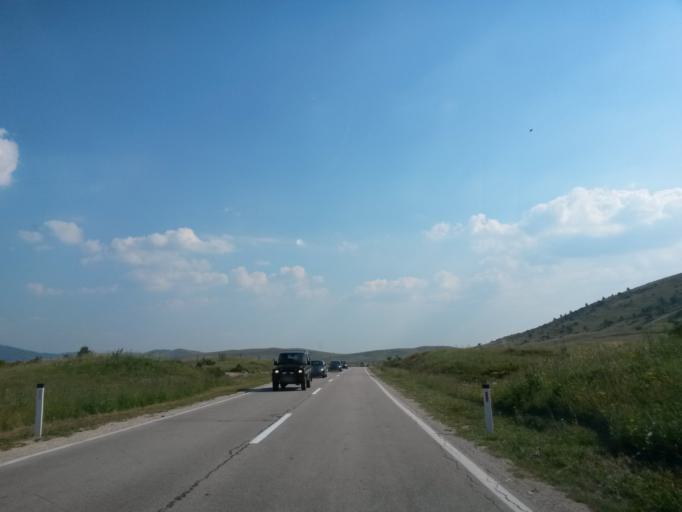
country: BA
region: Federation of Bosnia and Herzegovina
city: Tomislavgrad
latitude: 43.9163
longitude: 17.2049
